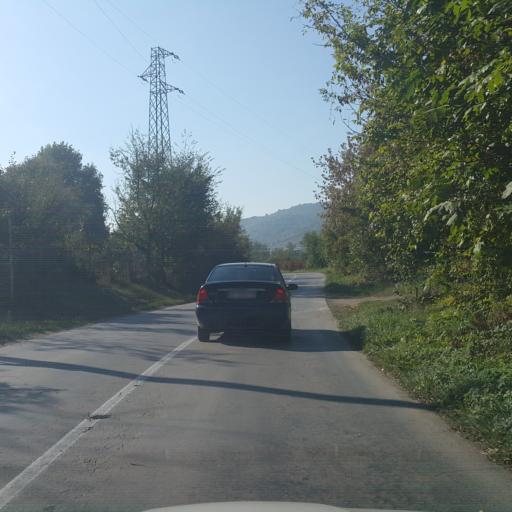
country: RS
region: Central Serbia
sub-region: Pirotski Okrug
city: Pirot
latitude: 43.1916
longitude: 22.5673
